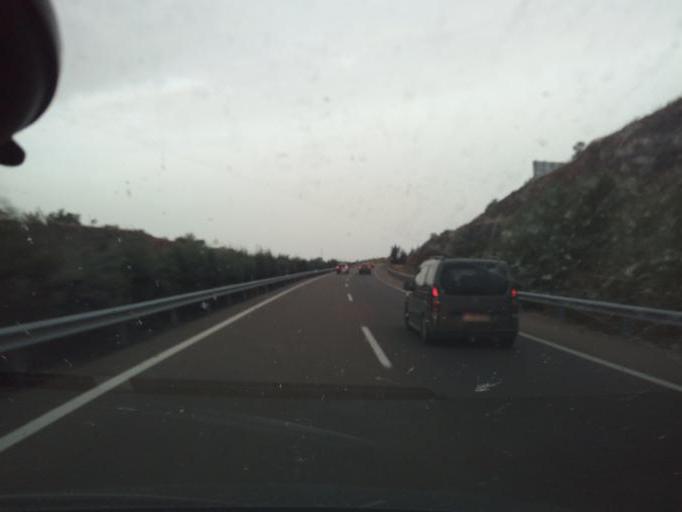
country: ES
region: Extremadura
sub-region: Provincia de Badajoz
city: San Pedro de Merida
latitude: 38.9462
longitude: -6.1866
